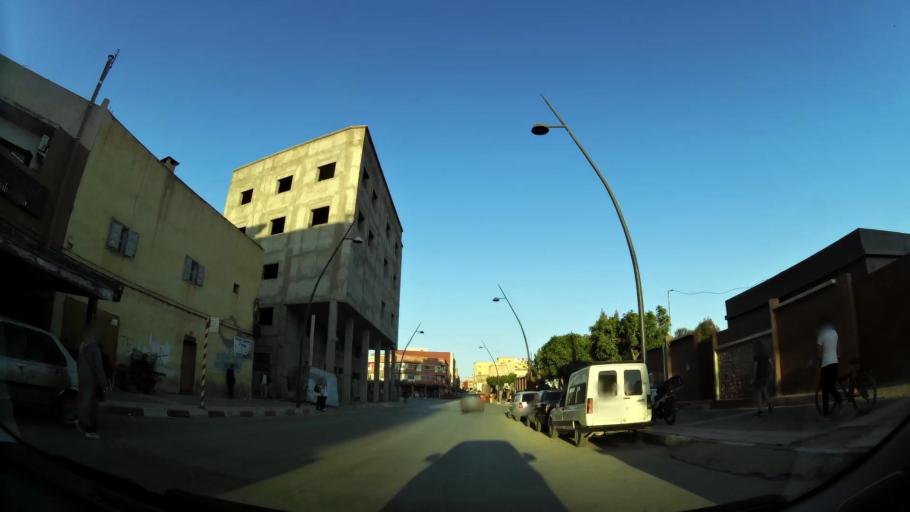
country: MA
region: Oriental
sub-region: Berkane-Taourirt
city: Berkane
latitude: 34.9214
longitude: -2.3312
